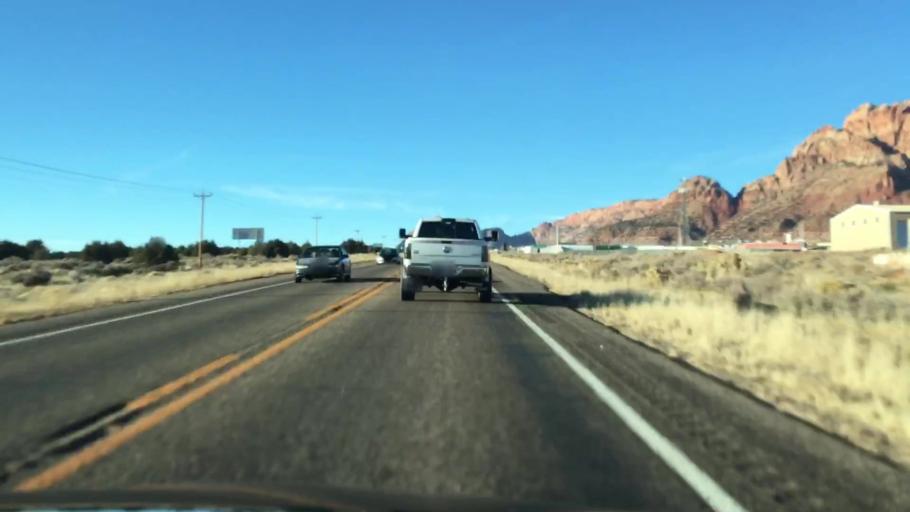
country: US
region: Arizona
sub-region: Mohave County
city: Colorado City
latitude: 36.9953
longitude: -112.9951
